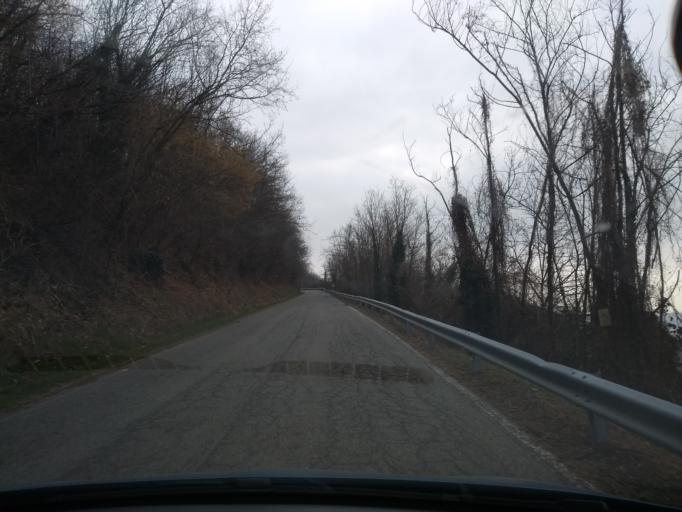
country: IT
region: Piedmont
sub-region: Provincia di Torino
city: Palazzo Canavese
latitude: 45.4707
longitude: 7.9804
